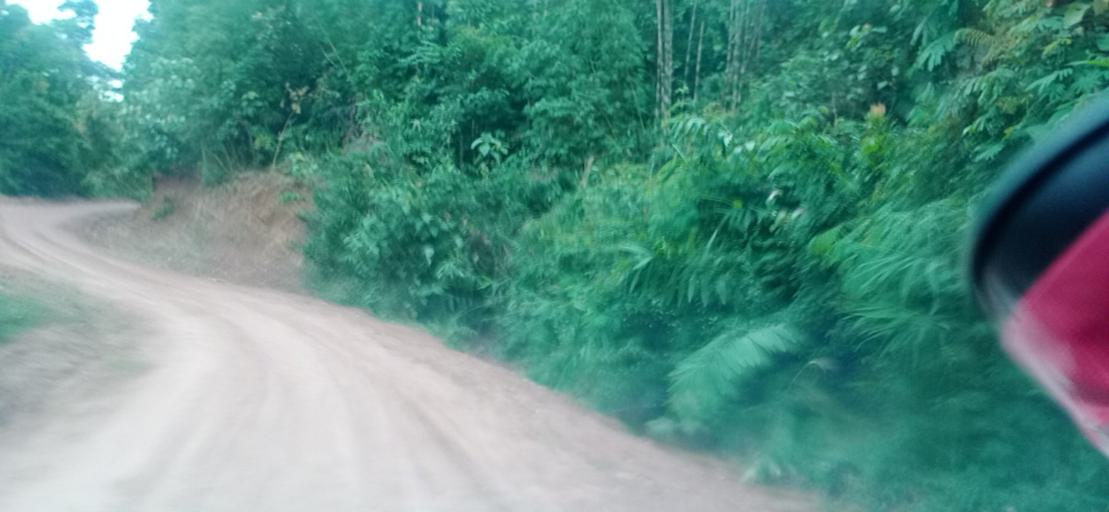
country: TH
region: Changwat Bueng Kan
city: Pak Khat
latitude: 18.5517
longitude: 103.4265
